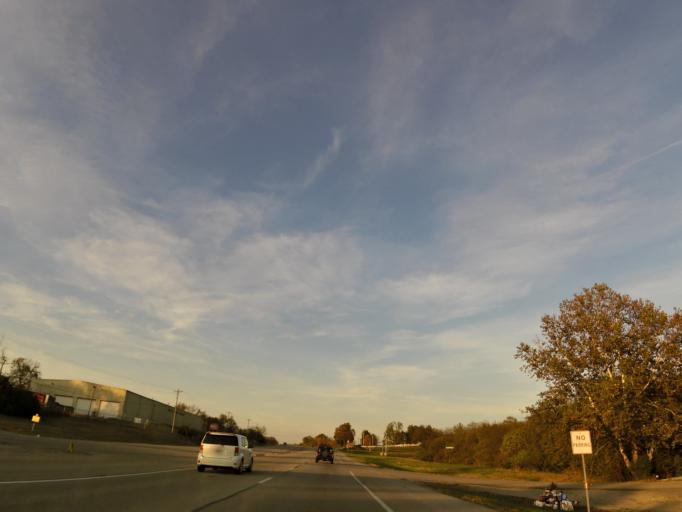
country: US
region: Kentucky
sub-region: Jessamine County
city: Wilmore
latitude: 37.7848
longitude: -84.6075
